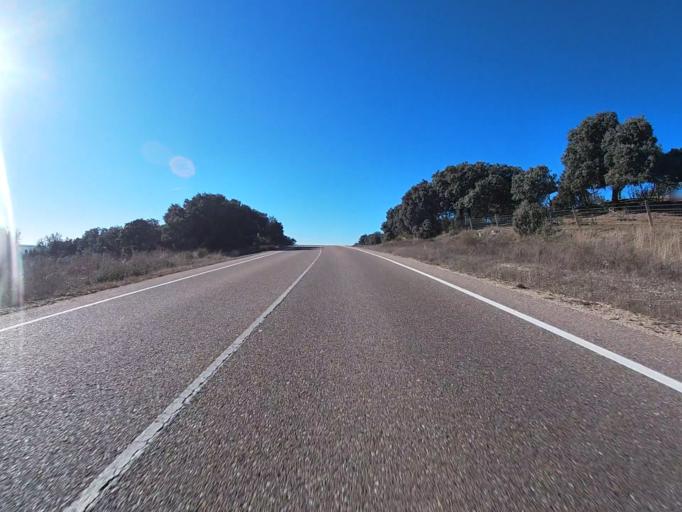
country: ES
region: Castille and Leon
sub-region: Provincia de Salamanca
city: Juzbado
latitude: 41.0782
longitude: -5.8468
